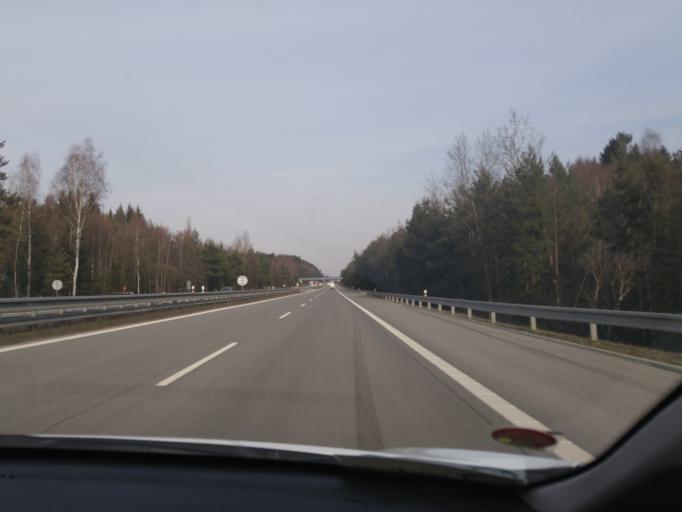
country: CZ
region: Central Bohemia
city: Cechtice
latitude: 49.6206
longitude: 15.1344
